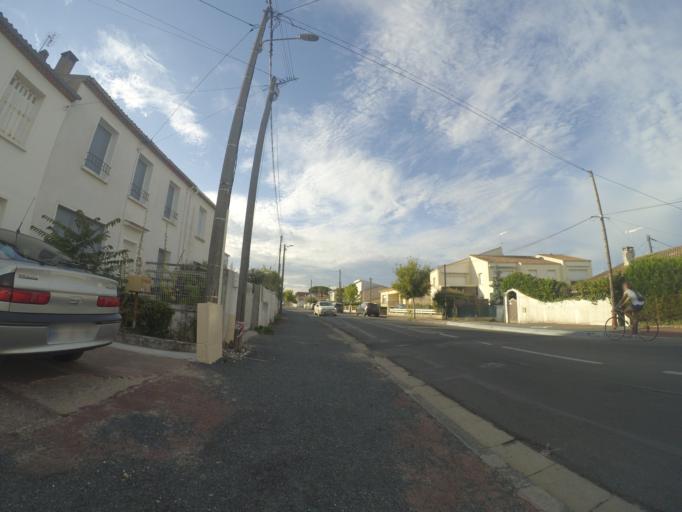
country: FR
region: Poitou-Charentes
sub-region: Departement de la Charente-Maritime
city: Saint-Georges-de-Didonne
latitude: 45.6031
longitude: -1.0031
